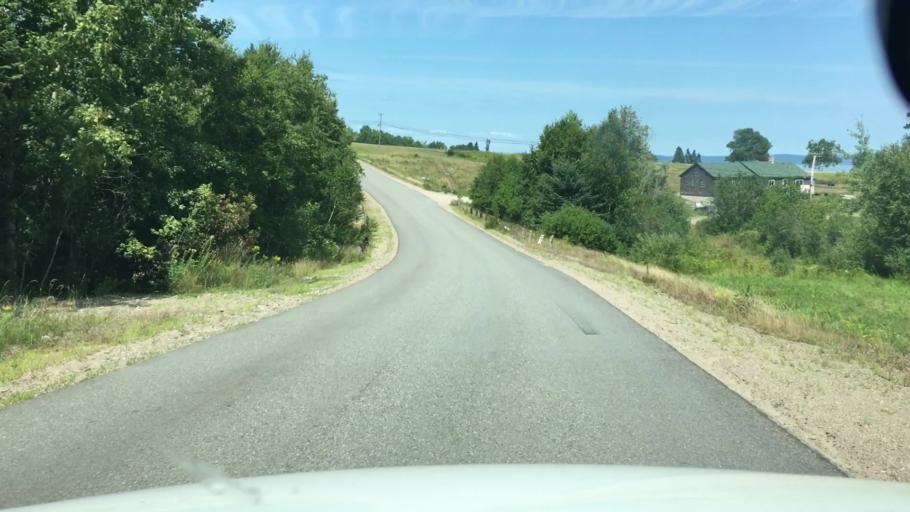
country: CA
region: New Brunswick
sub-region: Charlotte County
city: Saint Andrews
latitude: 44.9931
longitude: -67.0656
